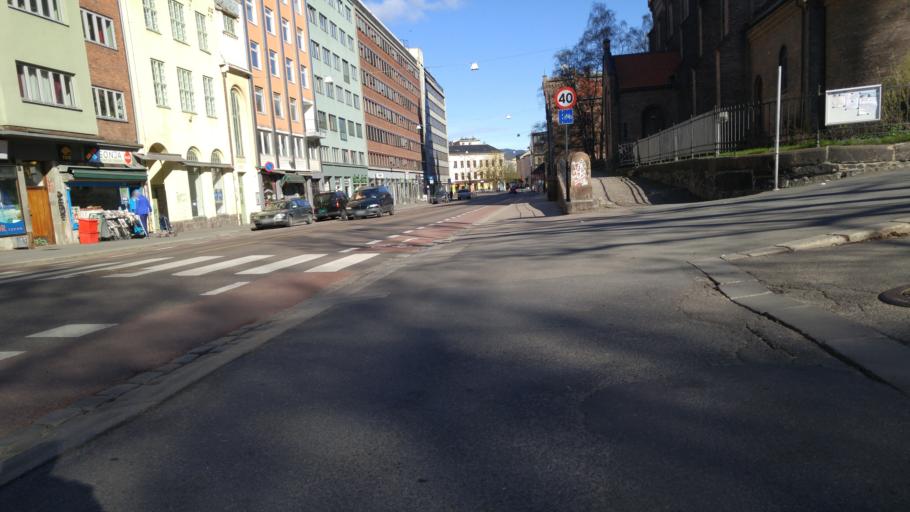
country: NO
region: Oslo
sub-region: Oslo
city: Oslo
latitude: 59.9106
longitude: 10.7677
